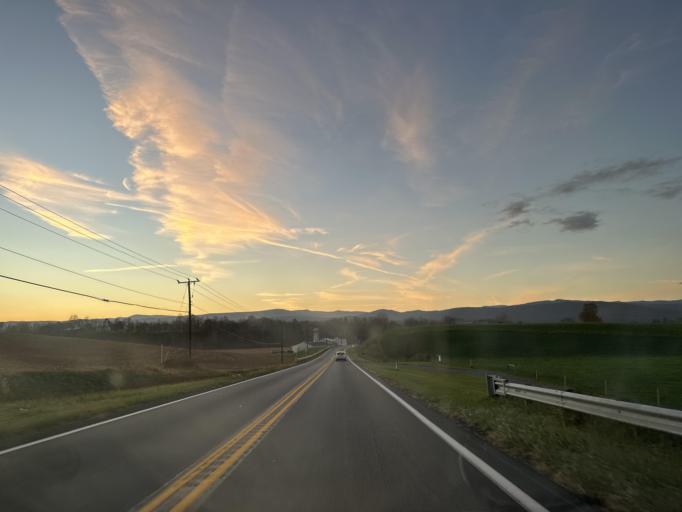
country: US
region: Virginia
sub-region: Rockingham County
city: Bridgewater
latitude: 38.4271
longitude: -79.0309
